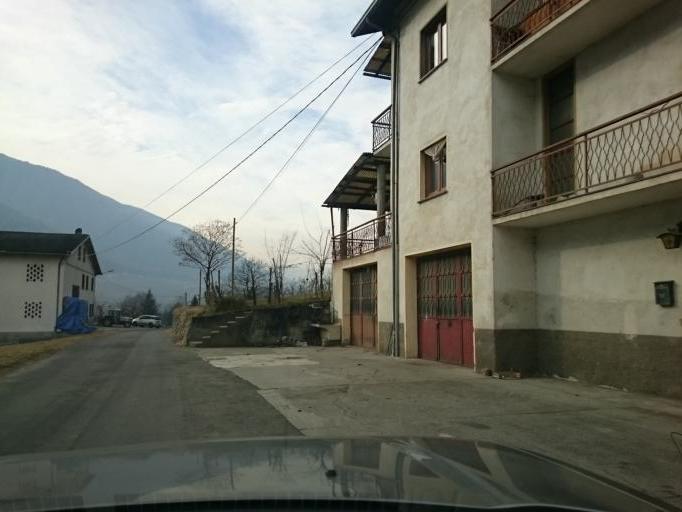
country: IT
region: Lombardy
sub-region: Provincia di Sondrio
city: Lovero
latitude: 46.2392
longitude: 10.2264
